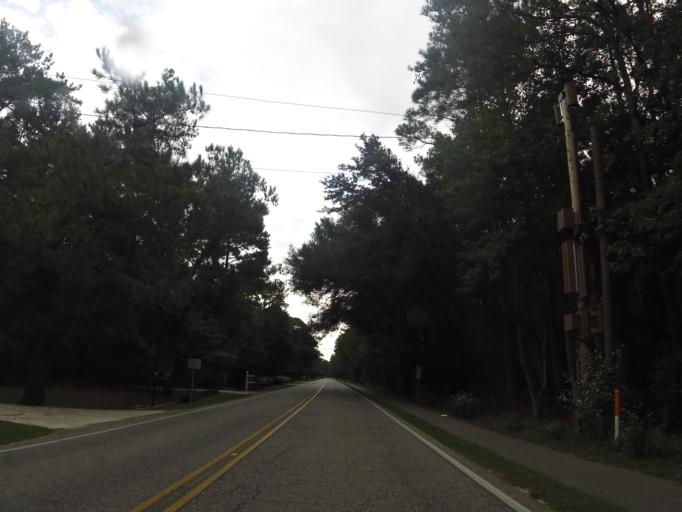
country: US
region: Alabama
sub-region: Baldwin County
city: Point Clear
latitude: 30.4980
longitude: -87.9234
